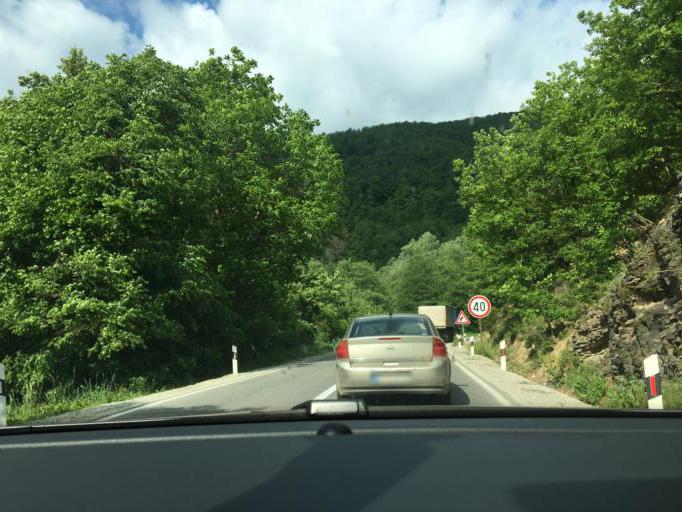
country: MK
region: Resen
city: Jankovec
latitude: 41.1396
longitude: 21.0031
